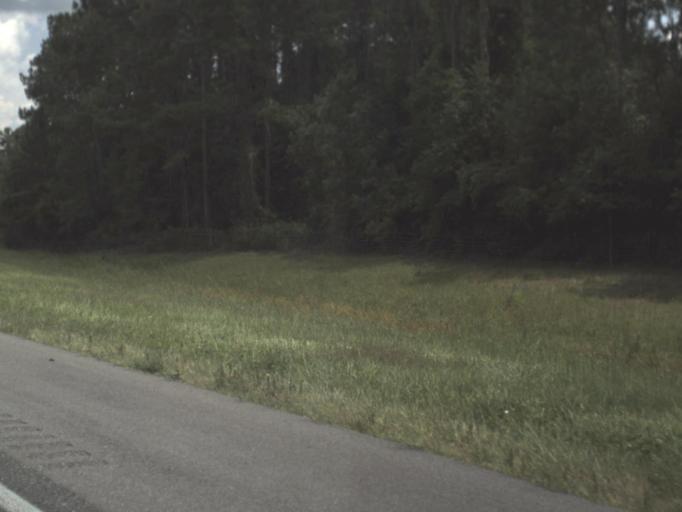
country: US
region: Florida
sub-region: Suwannee County
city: Wellborn
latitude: 30.3673
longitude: -82.8568
